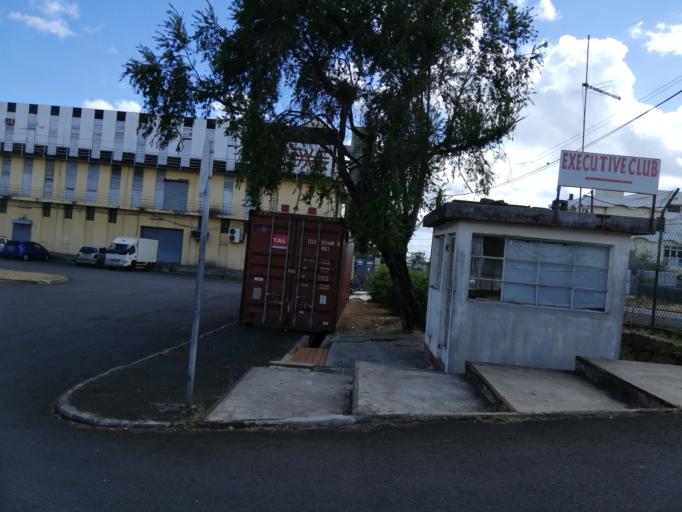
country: MU
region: Moka
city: Pailles
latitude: -20.1884
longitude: 57.4685
